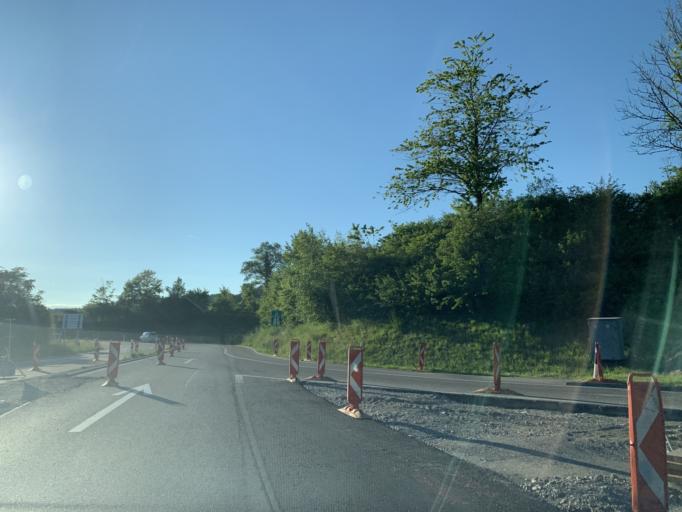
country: CH
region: Zurich
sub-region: Bezirk Winterthur
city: Oberwinterthur (Kreis 2)
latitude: 47.5314
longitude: 8.7751
